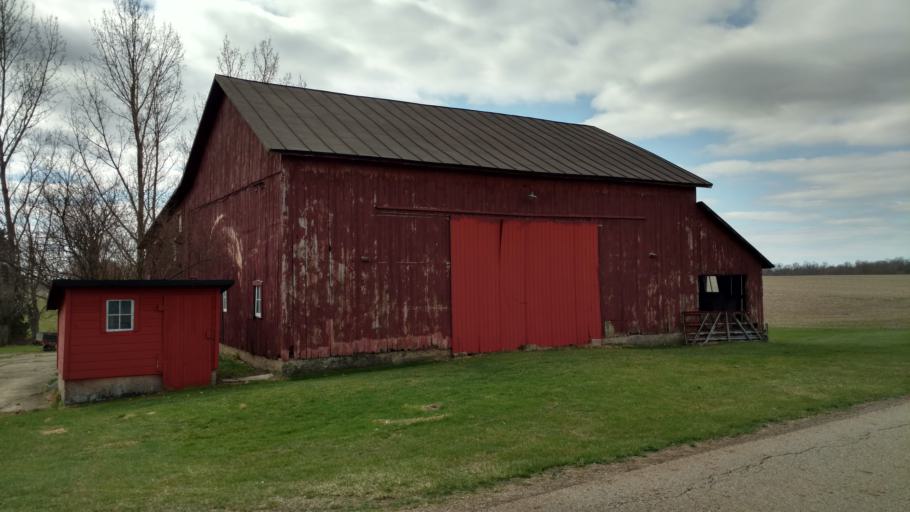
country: US
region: Ohio
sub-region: Knox County
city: Fredericktown
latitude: 40.4947
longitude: -82.4923
